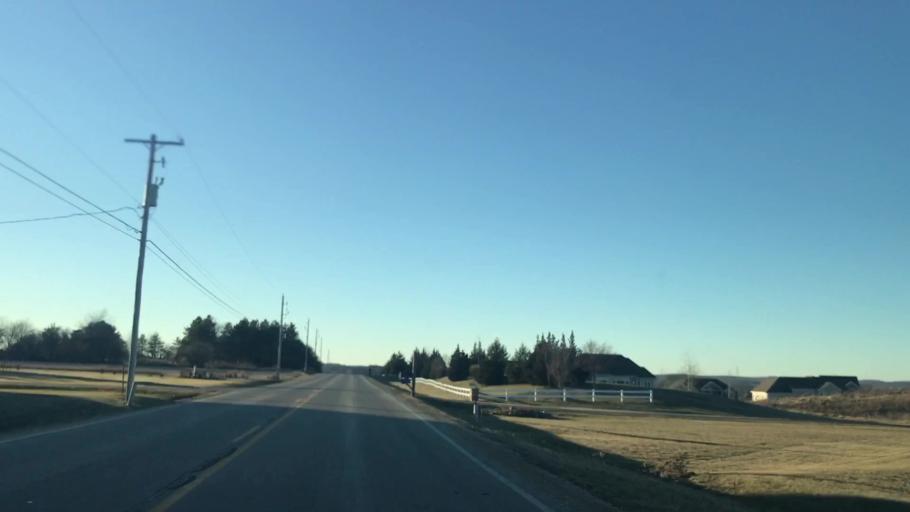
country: US
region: Wisconsin
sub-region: Washington County
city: Jackson
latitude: 43.2948
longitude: -88.1495
